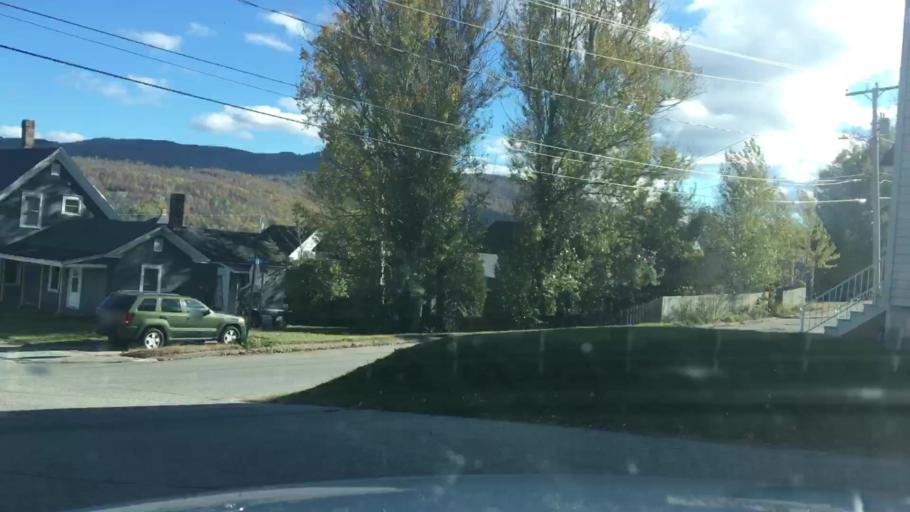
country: US
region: New Hampshire
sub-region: Coos County
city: Berlin
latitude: 44.4688
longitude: -71.1908
